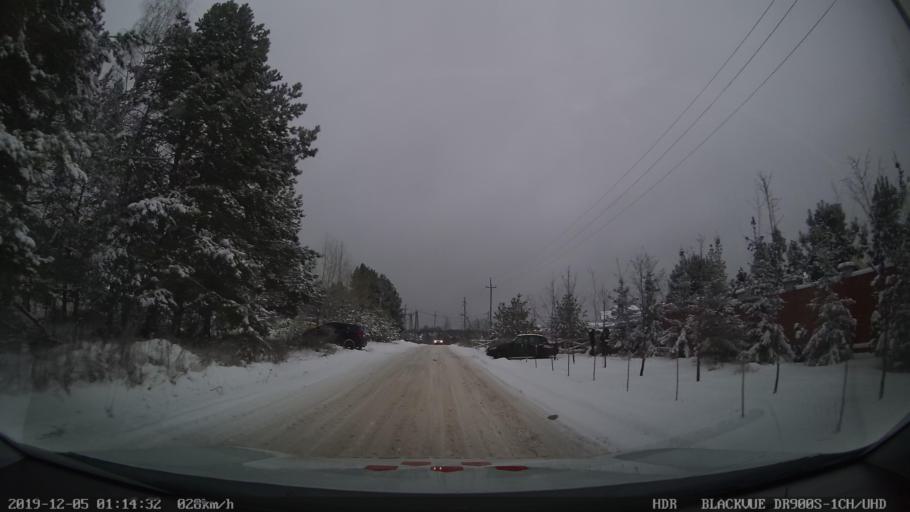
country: RU
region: Tatarstan
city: Stolbishchi
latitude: 55.6427
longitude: 49.1148
